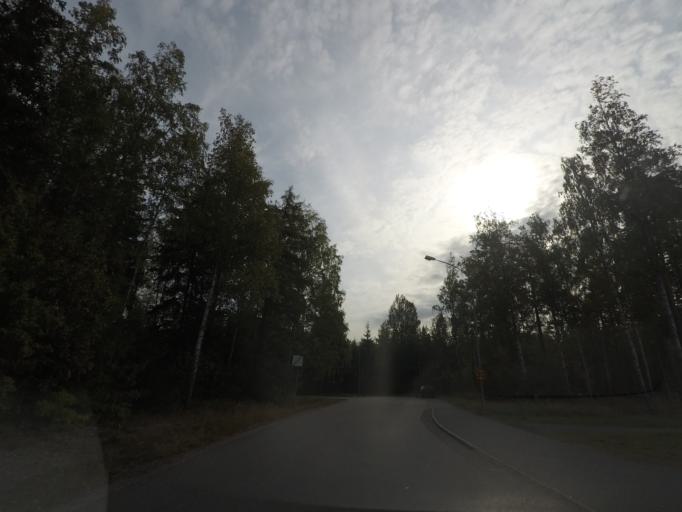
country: SE
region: Soedermanland
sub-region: Eskilstuna Kommun
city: Eskilstuna
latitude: 59.3617
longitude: 16.5468
